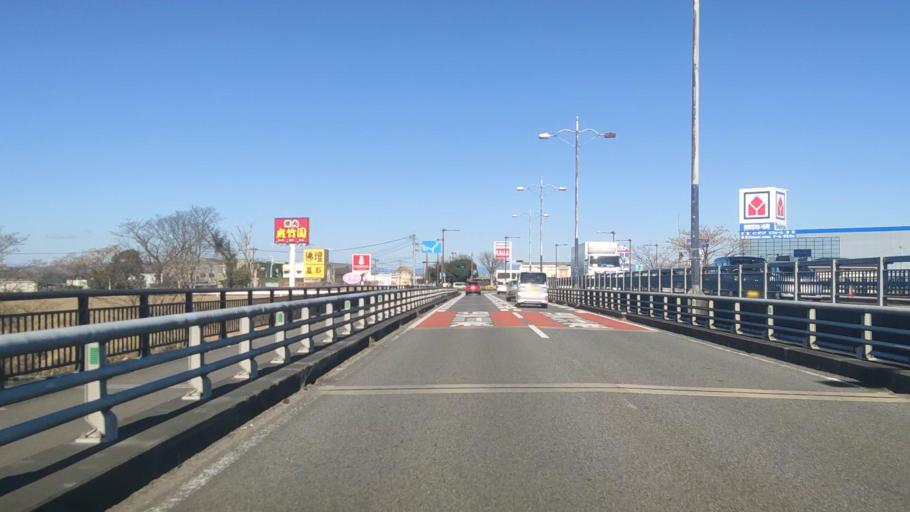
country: JP
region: Miyazaki
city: Miyakonojo
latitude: 31.7500
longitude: 131.0779
